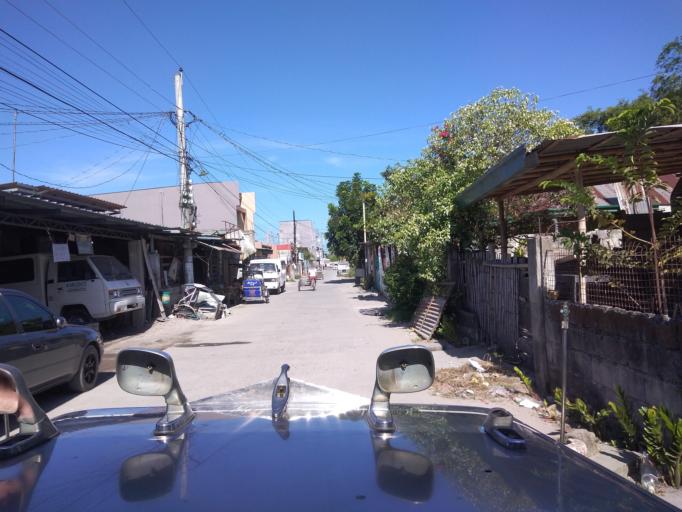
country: PH
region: Central Luzon
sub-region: Province of Pampanga
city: Calibutbut
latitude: 15.1001
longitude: 120.6054
